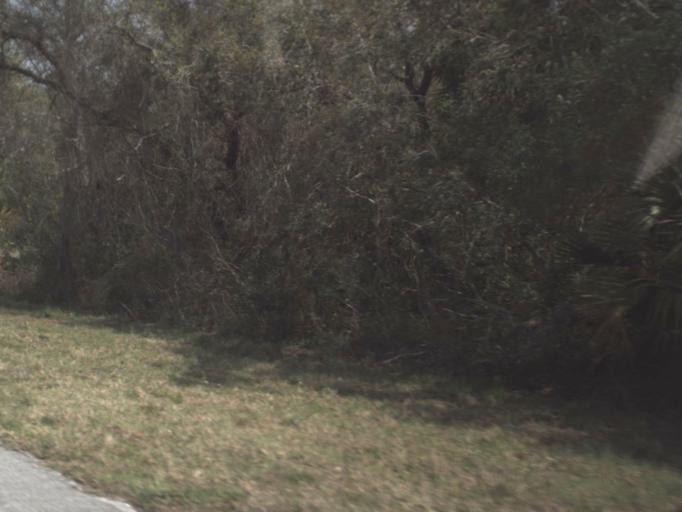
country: US
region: Florida
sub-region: Lake County
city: Astor
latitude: 29.1809
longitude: -81.6506
